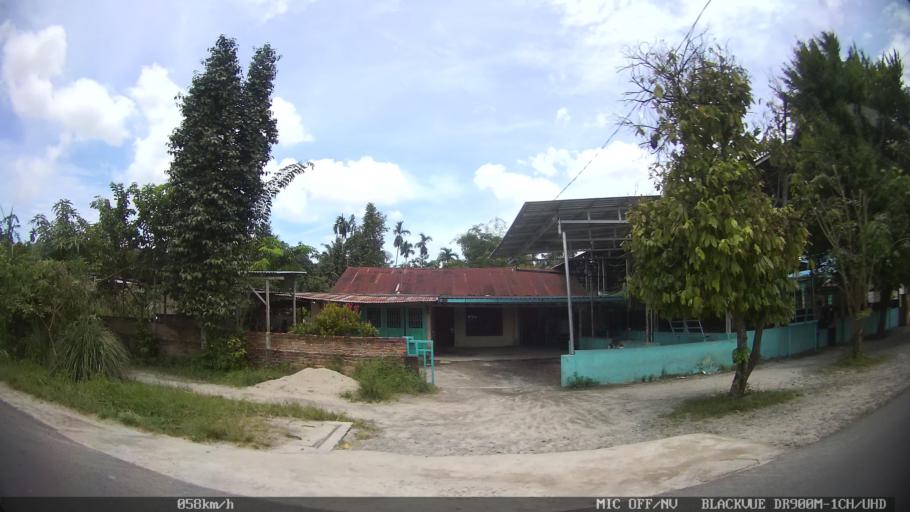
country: ID
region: North Sumatra
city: Percut
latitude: 3.5787
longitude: 98.8833
